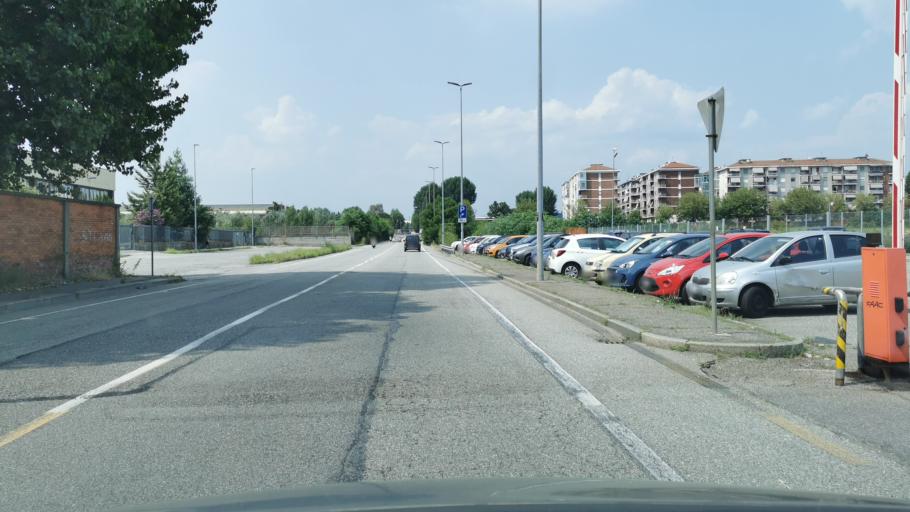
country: IT
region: Piedmont
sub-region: Provincia di Torino
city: Settimo Torinese
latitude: 45.1213
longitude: 7.7311
